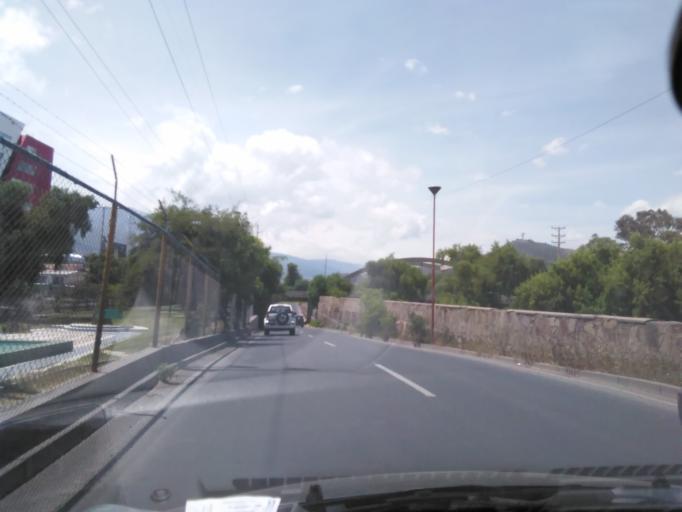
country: BO
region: Cochabamba
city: Cochabamba
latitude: -17.3807
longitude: -66.1581
